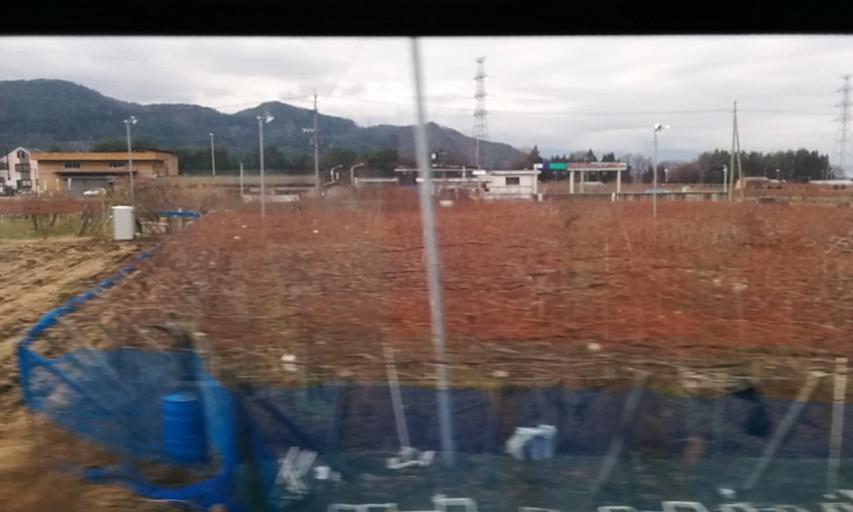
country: JP
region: Nagano
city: Shiojiri
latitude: 36.0944
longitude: 137.9249
